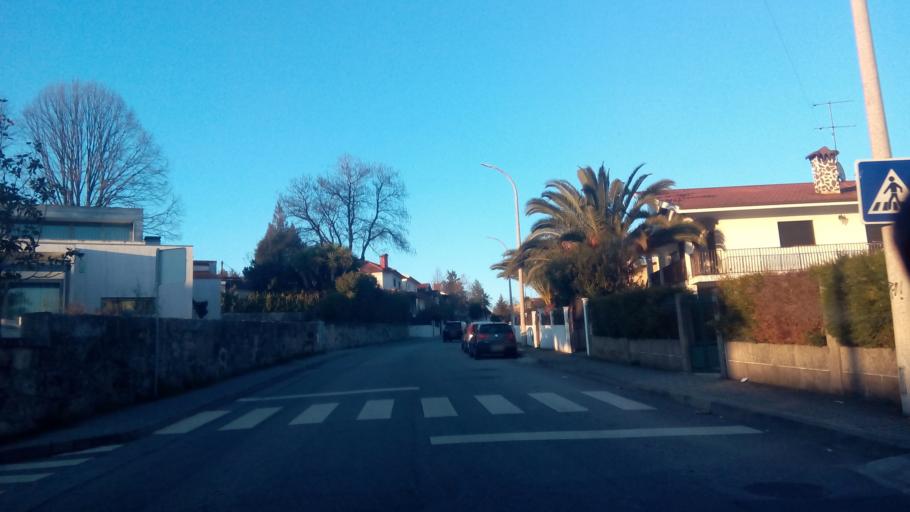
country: PT
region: Porto
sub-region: Amarante
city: Amarante
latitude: 41.2749
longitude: -8.0849
